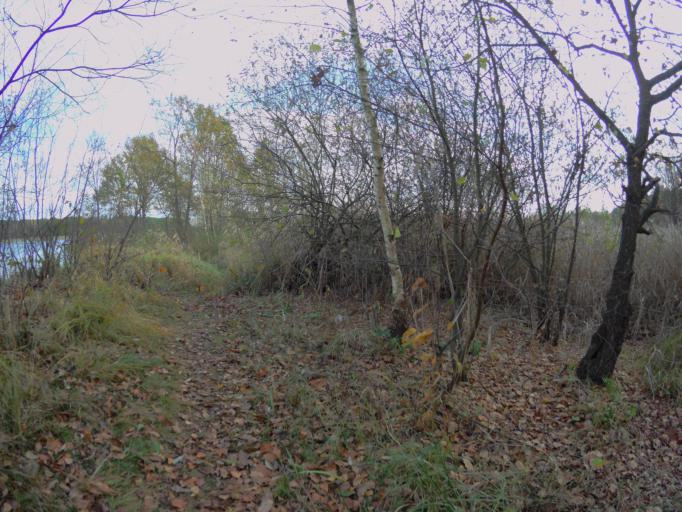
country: PL
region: Subcarpathian Voivodeship
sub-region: Powiat kolbuszowski
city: Lipnica
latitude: 50.3316
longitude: 21.9367
